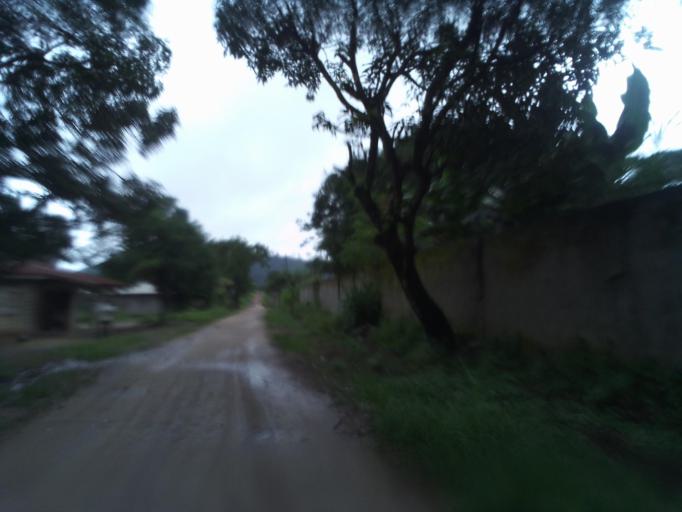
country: SL
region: Eastern Province
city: Kenema
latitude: 7.8531
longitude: -11.2085
